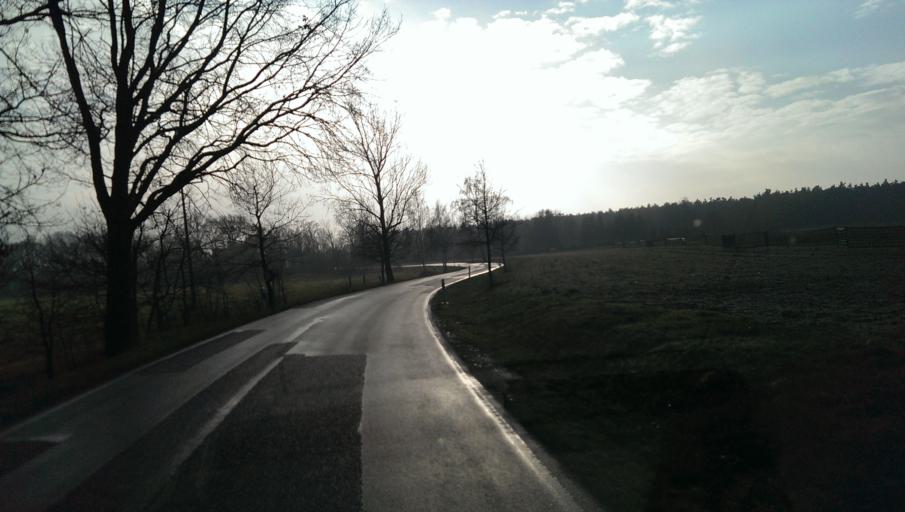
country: DE
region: Brandenburg
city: Bad Liebenwerda
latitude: 51.4836
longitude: 13.4201
